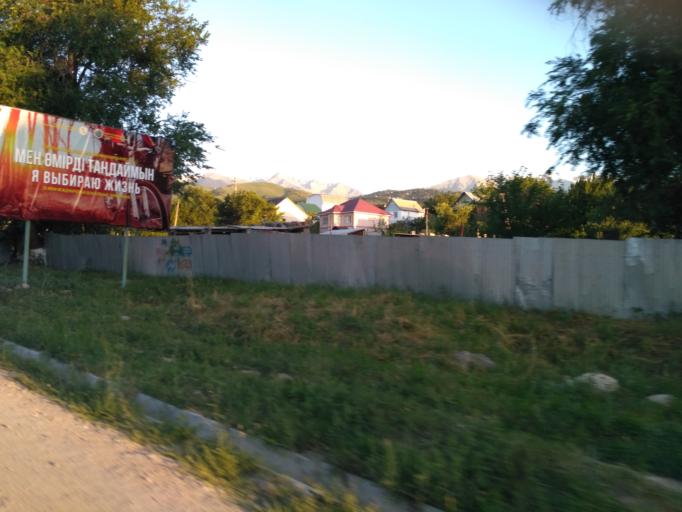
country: KZ
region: Almaty Qalasy
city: Almaty
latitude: 43.1721
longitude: 76.7702
